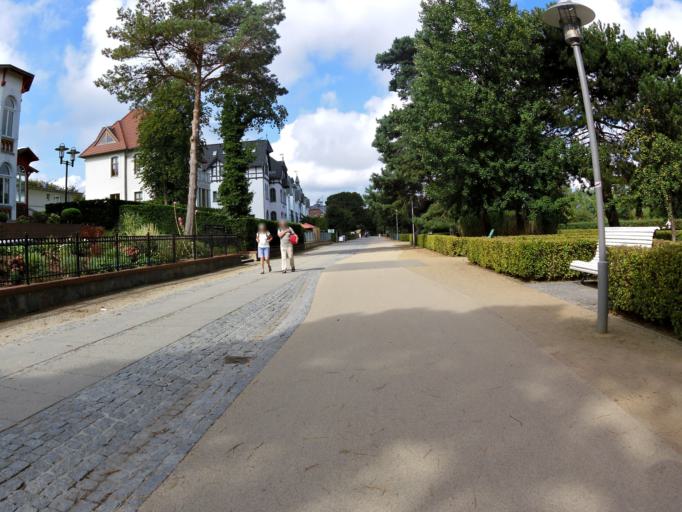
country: DE
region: Mecklenburg-Vorpommern
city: Ostseebad Zinnowitz
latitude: 54.0792
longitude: 13.9209
